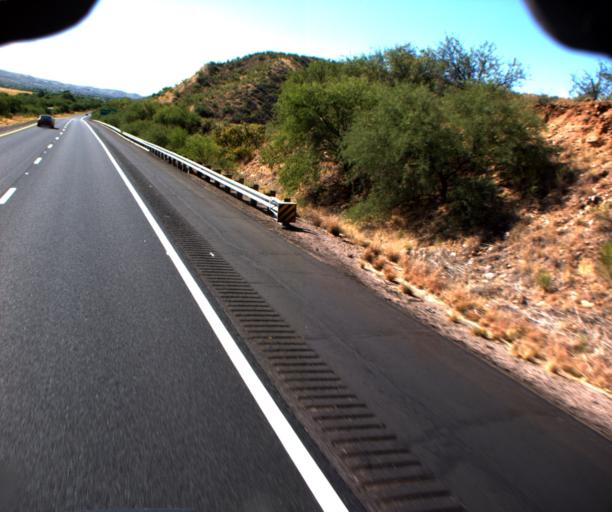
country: US
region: Arizona
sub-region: Santa Cruz County
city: Tubac
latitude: 31.5440
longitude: -111.0442
